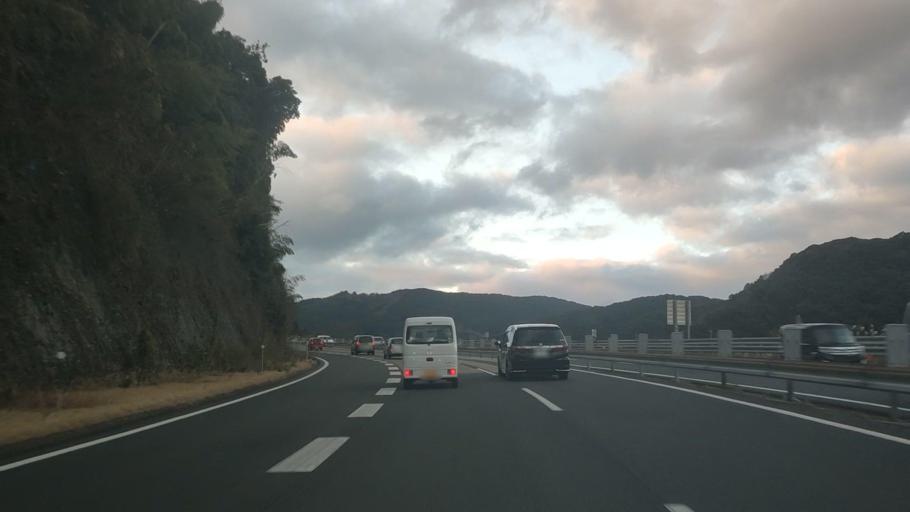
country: JP
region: Nagasaki
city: Obita
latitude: 32.8158
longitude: 129.9566
